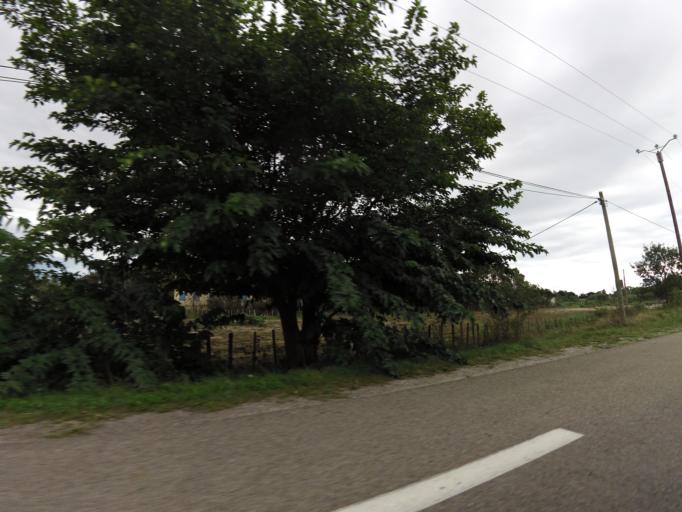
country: FR
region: Languedoc-Roussillon
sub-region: Departement du Gard
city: Le Grau-du-Roi
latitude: 43.5614
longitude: 4.1575
